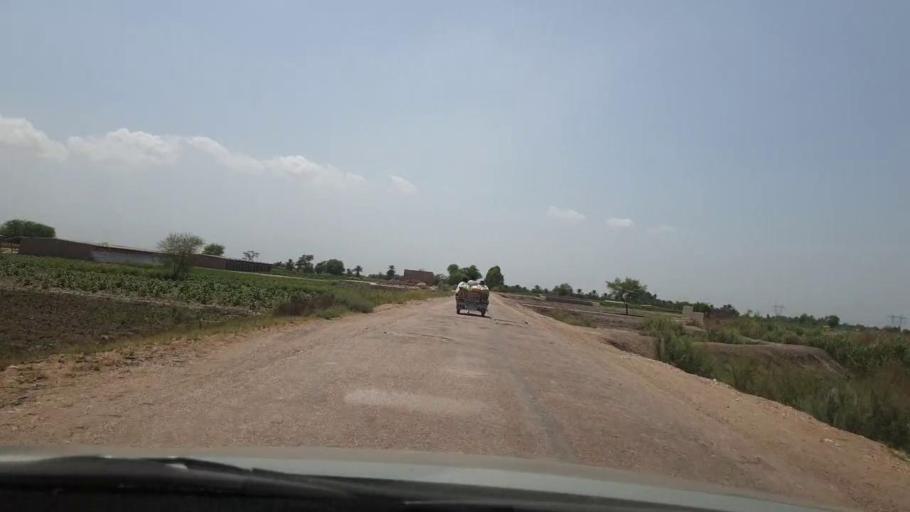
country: PK
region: Sindh
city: Rohri
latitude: 27.6695
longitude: 69.0658
